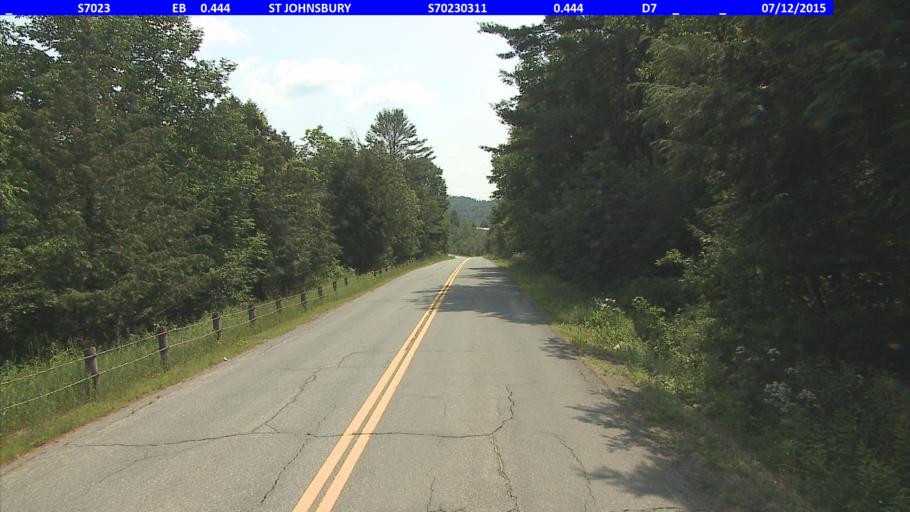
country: US
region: Vermont
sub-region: Caledonia County
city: St Johnsbury
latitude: 44.4451
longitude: -72.0545
